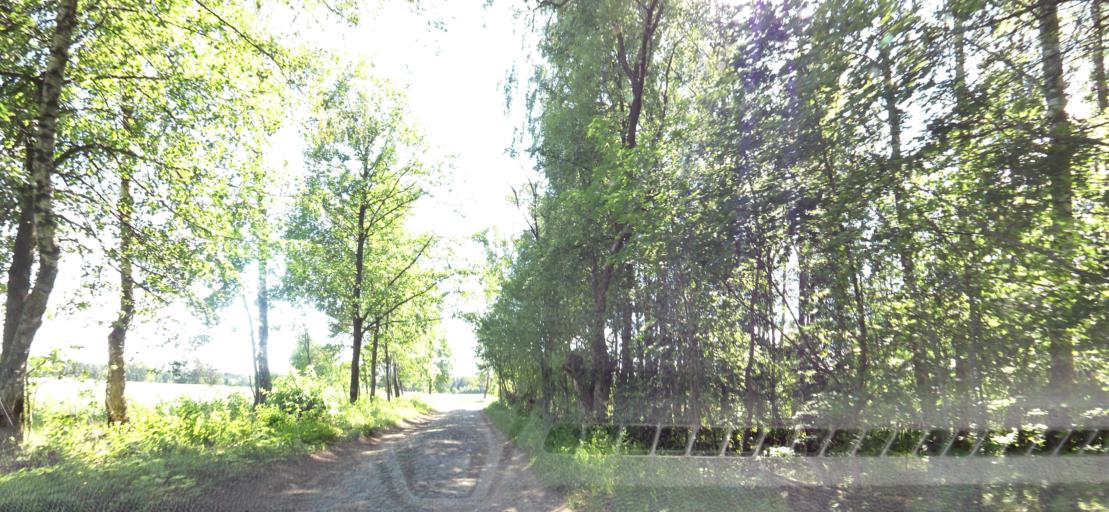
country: LT
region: Vilnius County
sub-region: Vilnius
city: Fabijoniskes
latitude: 54.8376
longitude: 25.3252
